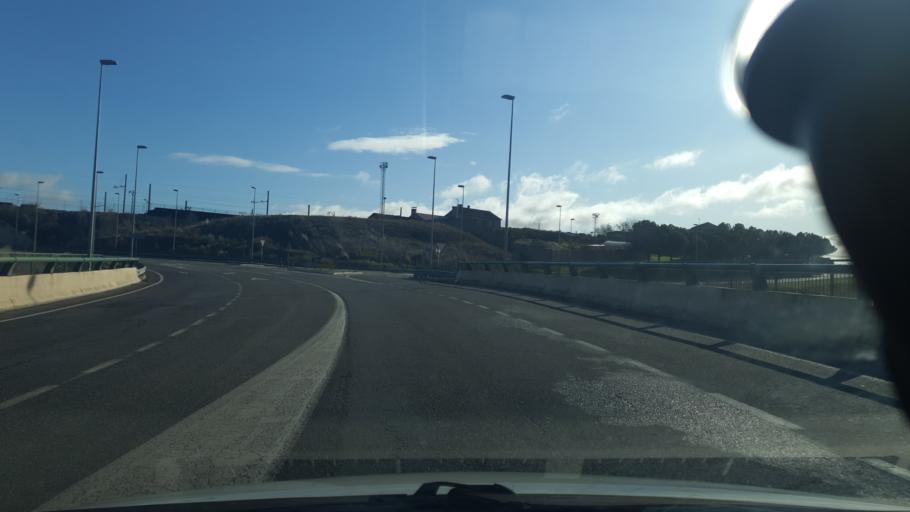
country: ES
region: Castille and Leon
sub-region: Provincia de Avila
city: Arevalo
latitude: 41.0493
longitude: -4.7050
